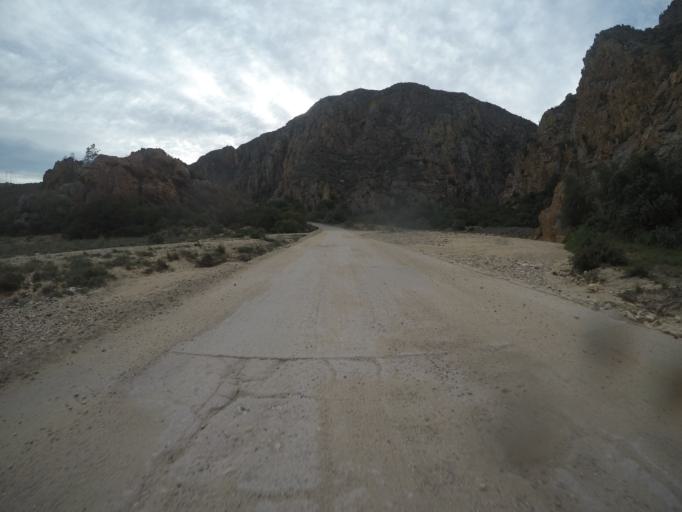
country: ZA
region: Eastern Cape
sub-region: Cacadu District Municipality
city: Willowmore
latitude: -33.5194
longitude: 23.6785
